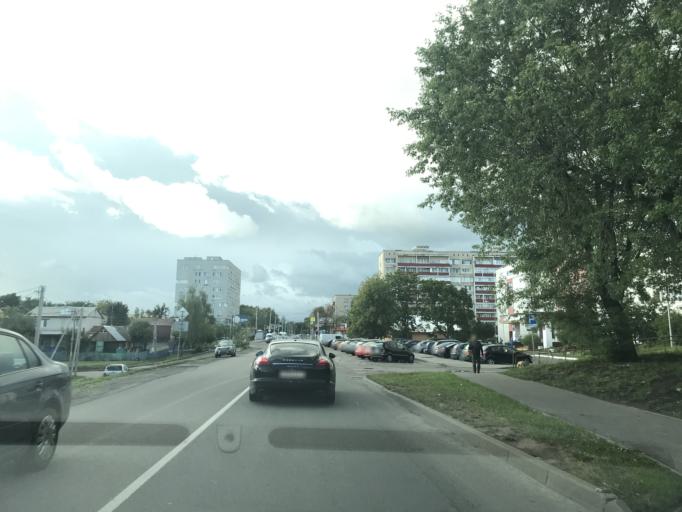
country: BY
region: Minsk
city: Minsk
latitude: 53.9507
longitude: 27.6014
